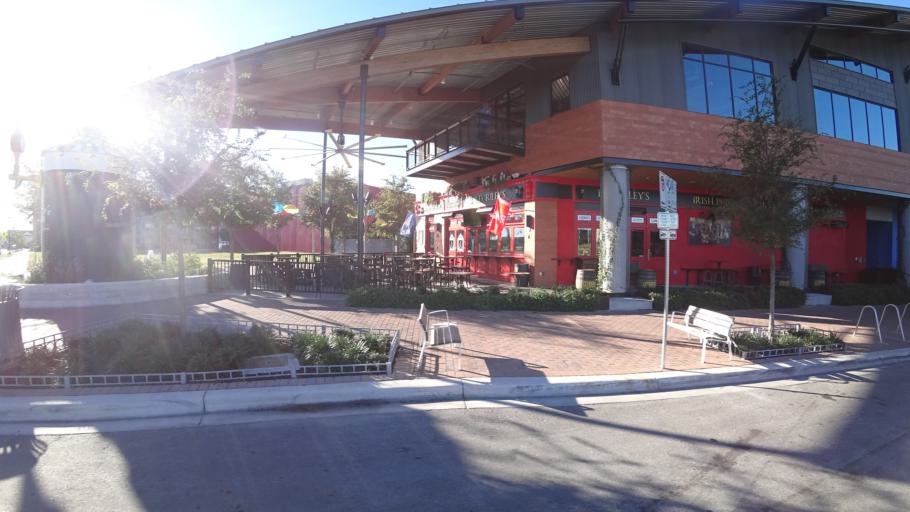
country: US
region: Texas
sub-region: Travis County
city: Austin
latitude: 30.2983
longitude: -97.7051
